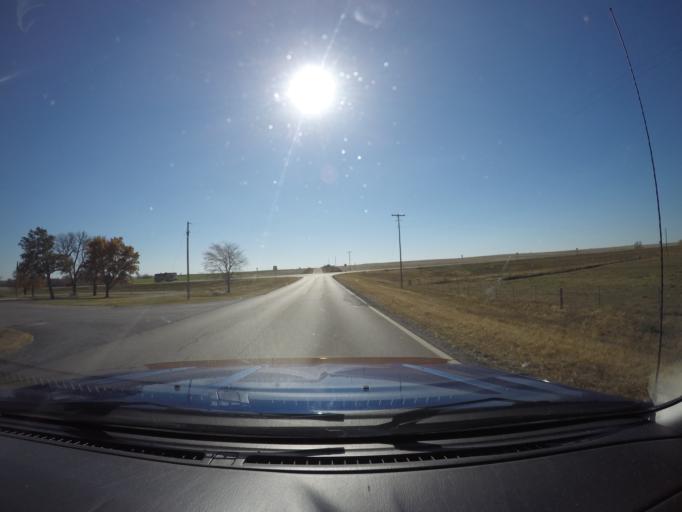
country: US
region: Kansas
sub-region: Nemaha County
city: Seneca
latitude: 39.8425
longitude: -96.2585
